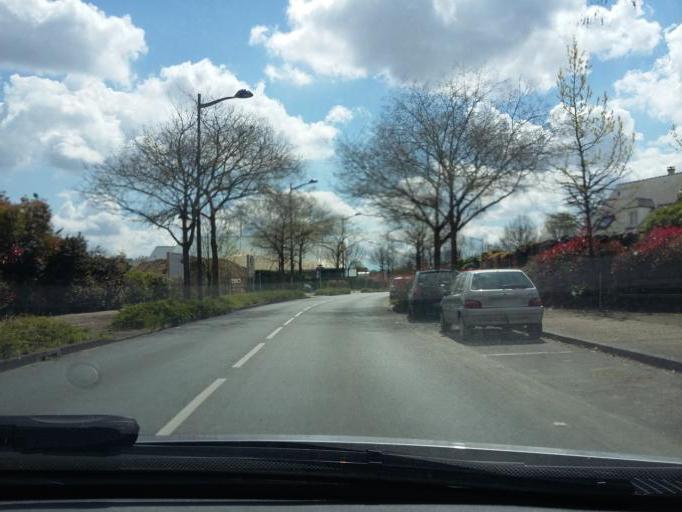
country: FR
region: Ile-de-France
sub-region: Departement du Val-d'Oise
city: Saint-Gratien
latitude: 48.9766
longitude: 2.2723
